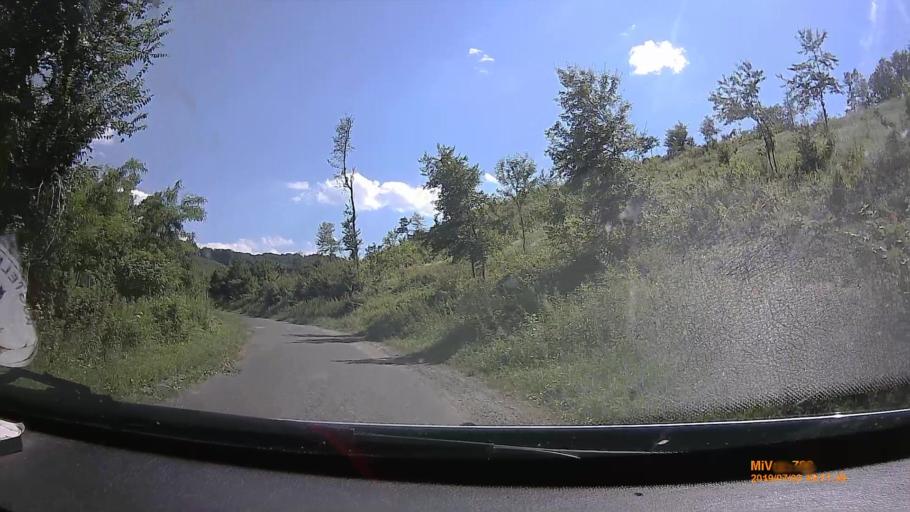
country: HU
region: Borsod-Abauj-Zemplen
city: Farkaslyuk
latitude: 48.2225
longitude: 20.3726
